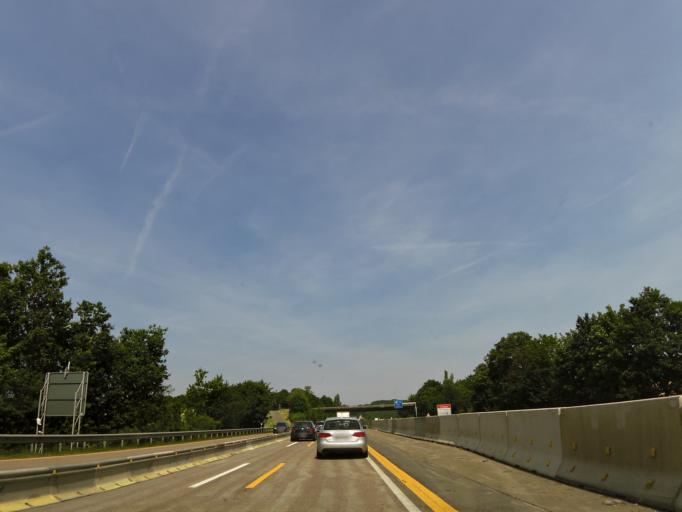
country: DE
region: Rheinland-Pfalz
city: Bell
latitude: 50.3944
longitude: 7.2468
